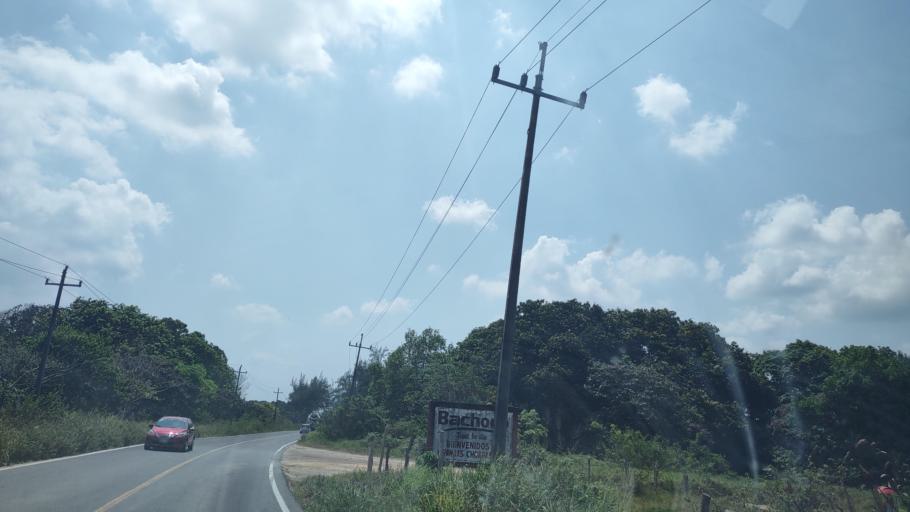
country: MX
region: Veracruz
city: Las Choapas
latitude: 17.9280
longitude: -94.1446
